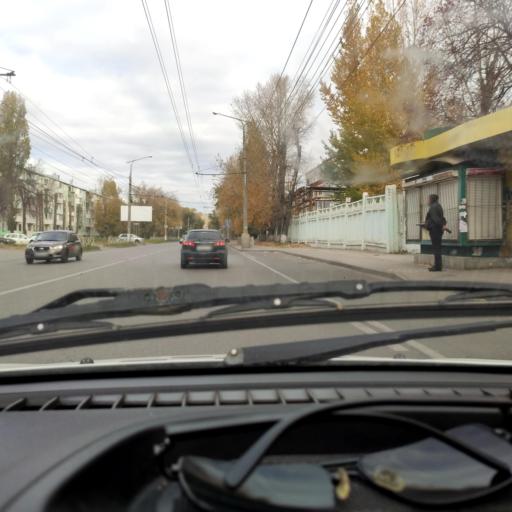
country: RU
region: Samara
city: Tol'yatti
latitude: 53.5124
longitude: 49.4299
